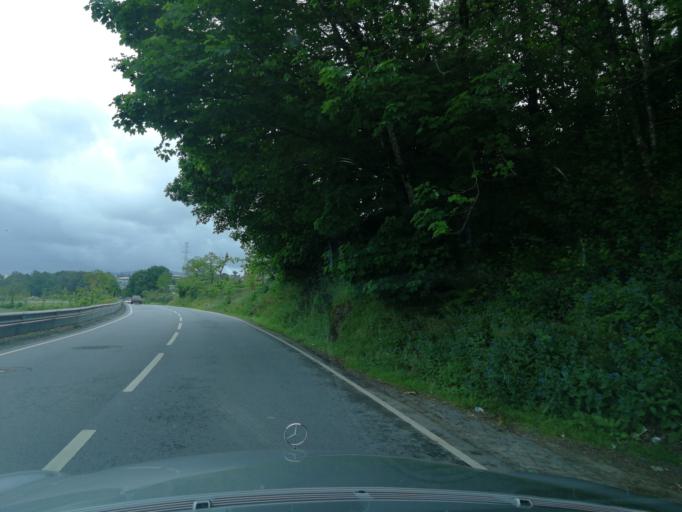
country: PT
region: Braga
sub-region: Braga
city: Adaufe
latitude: 41.6027
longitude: -8.4201
